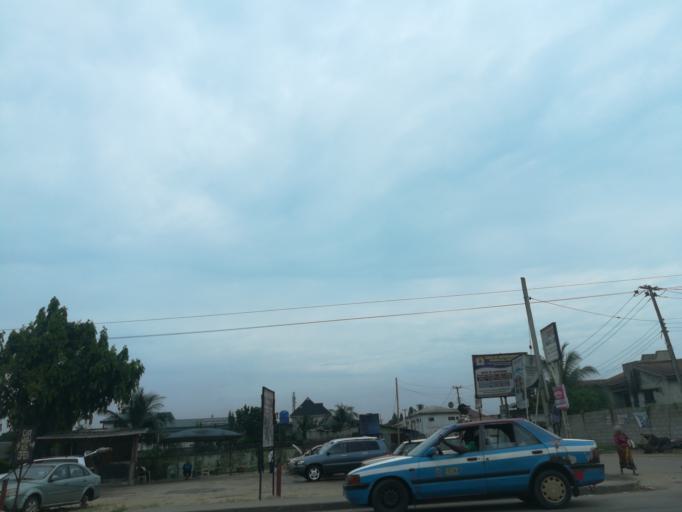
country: NG
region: Rivers
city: Port Harcourt
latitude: 4.8437
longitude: 6.9831
